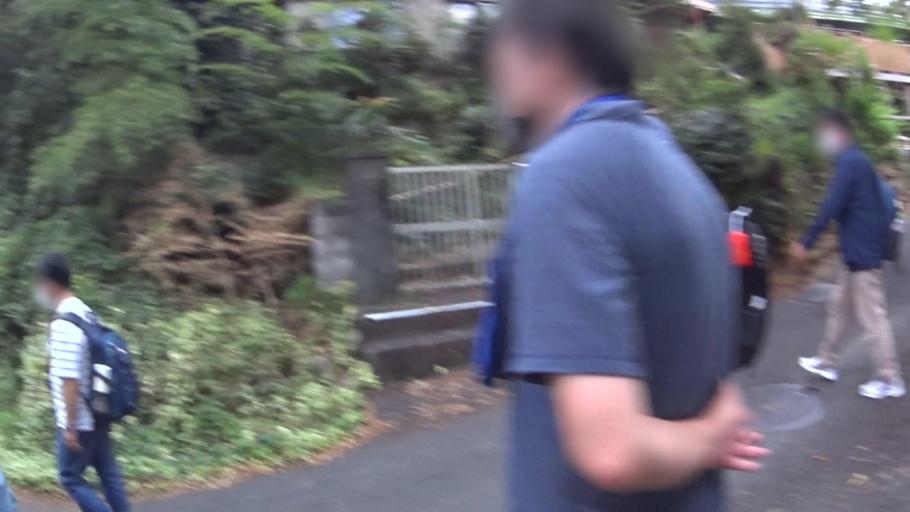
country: JP
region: Gifu
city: Tarui
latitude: 35.3028
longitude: 136.4387
